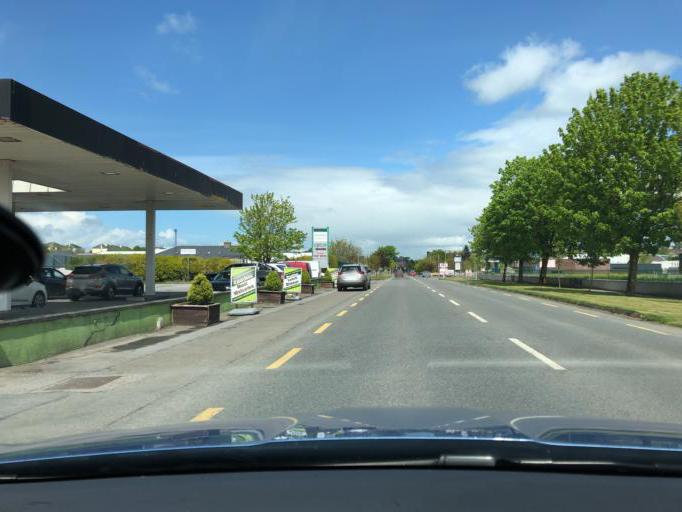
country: IE
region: Munster
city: Cashel
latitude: 52.5068
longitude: -7.8911
